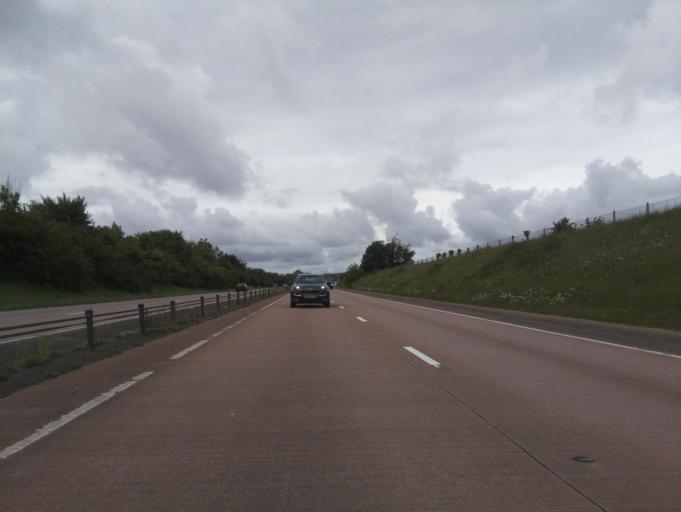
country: GB
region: England
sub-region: Devon
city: Ottery St Mary
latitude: 50.7745
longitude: -3.2770
